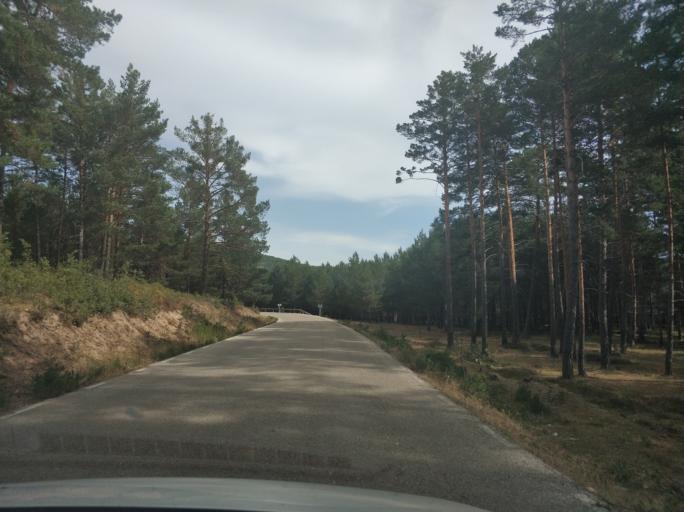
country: ES
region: Castille and Leon
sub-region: Provincia de Soria
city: Navaleno
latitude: 41.8767
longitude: -2.9376
